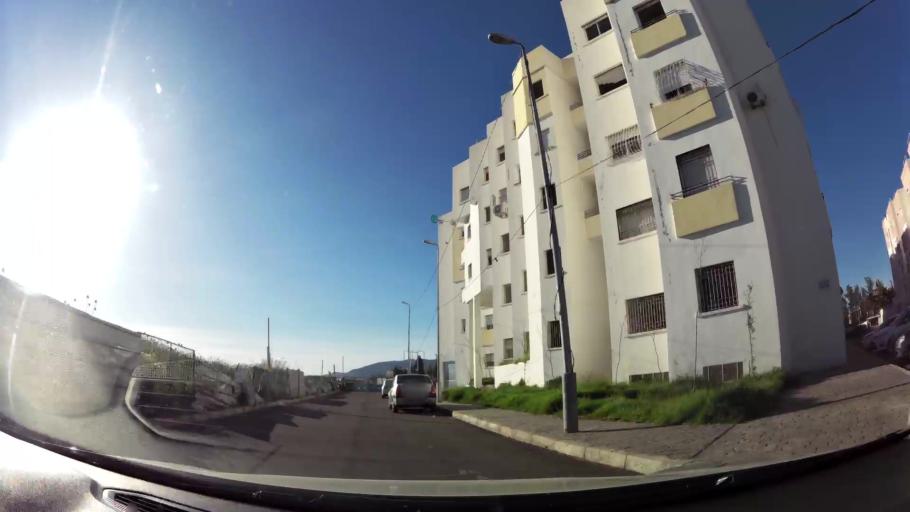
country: MA
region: Fes-Boulemane
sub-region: Fes
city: Fes
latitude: 34.0119
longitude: -5.0142
